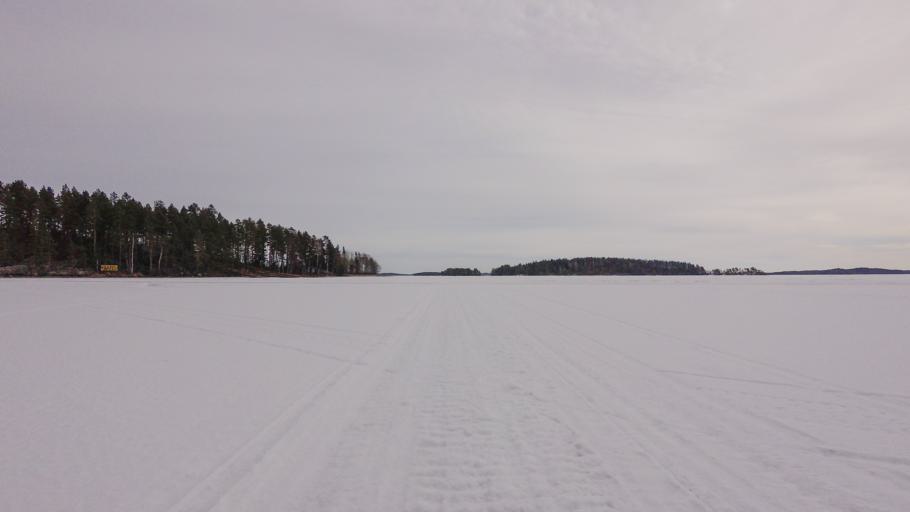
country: FI
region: Southern Savonia
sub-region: Savonlinna
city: Rantasalmi
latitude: 62.1140
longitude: 28.3360
